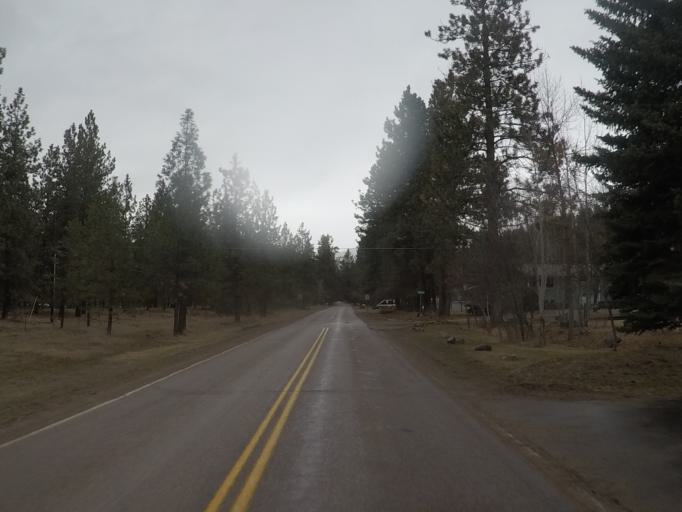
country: US
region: Montana
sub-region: Missoula County
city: East Missoula
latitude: 46.9089
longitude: -113.9604
